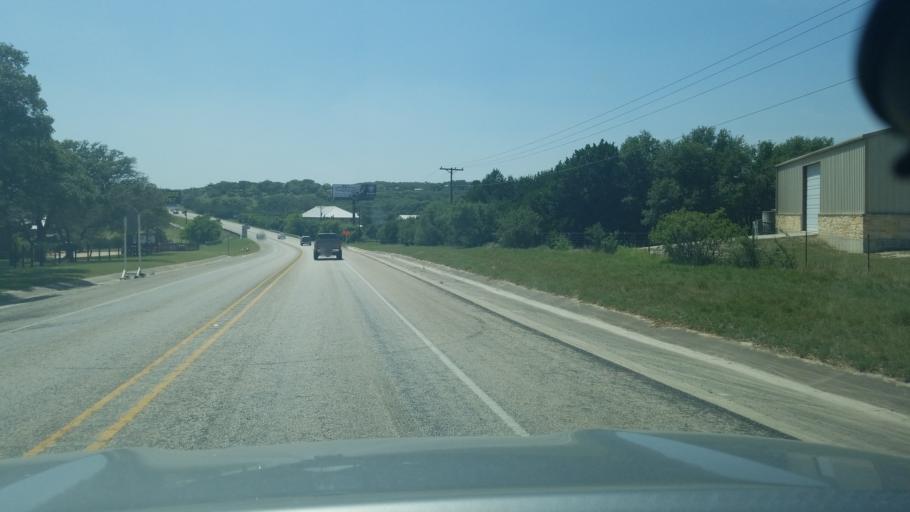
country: US
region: Texas
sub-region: Bexar County
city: Fair Oaks Ranch
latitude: 29.8155
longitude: -98.6145
